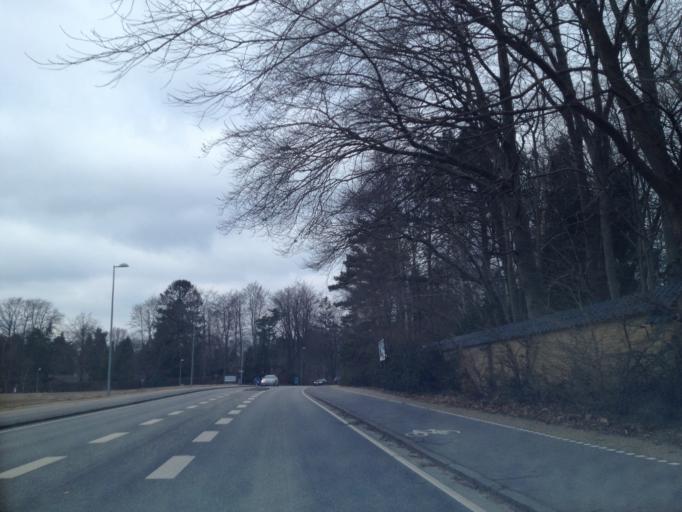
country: DK
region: Capital Region
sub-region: Rudersdal Kommune
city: Trorod
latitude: 55.8668
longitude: 12.5512
